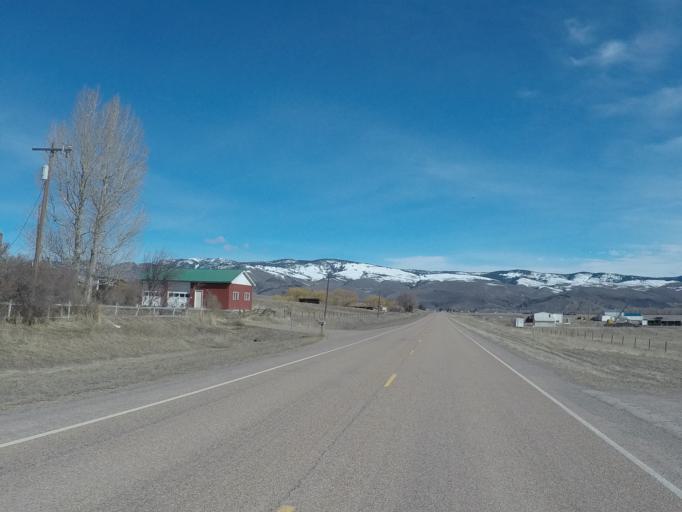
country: US
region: Montana
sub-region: Granite County
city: Philipsburg
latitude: 46.6347
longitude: -113.1692
